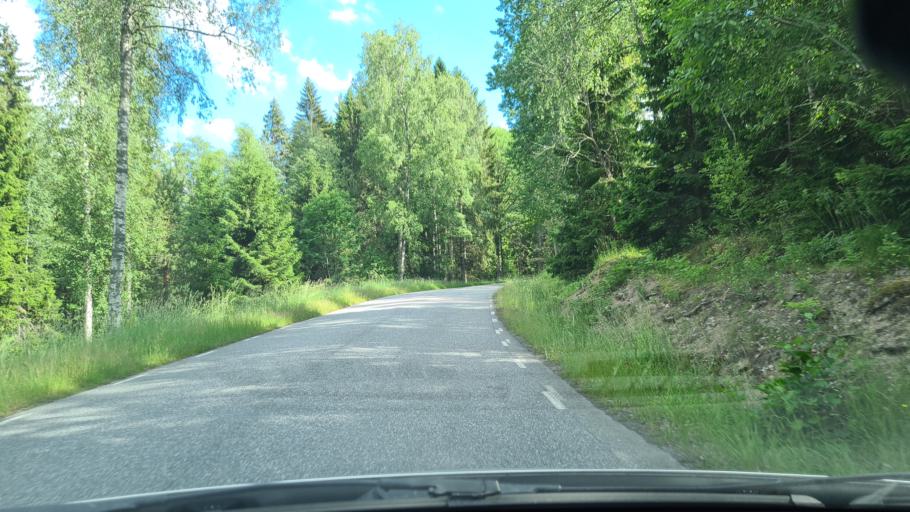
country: SE
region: Stockholm
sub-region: Varmdo Kommun
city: Mortnas
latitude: 59.4020
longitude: 18.4621
